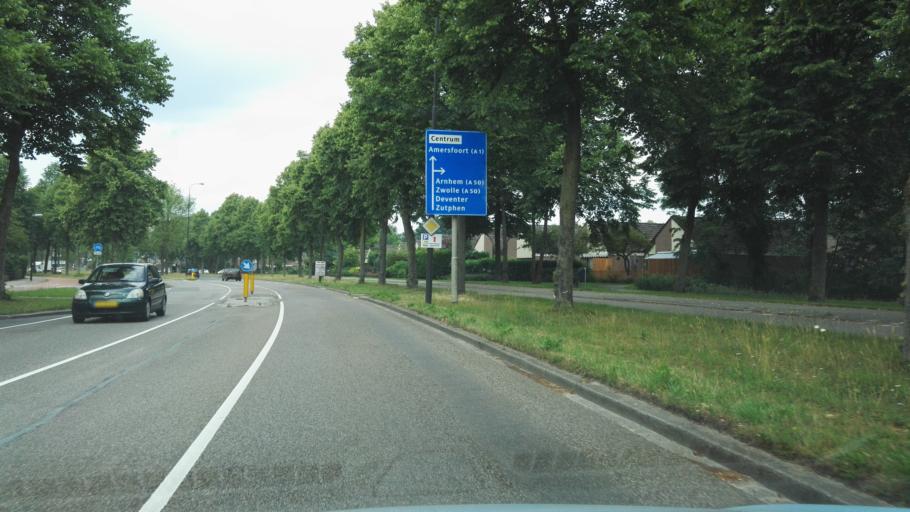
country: NL
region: Gelderland
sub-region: Gemeente Apeldoorn
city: Apeldoorn
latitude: 52.2012
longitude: 6.0006
